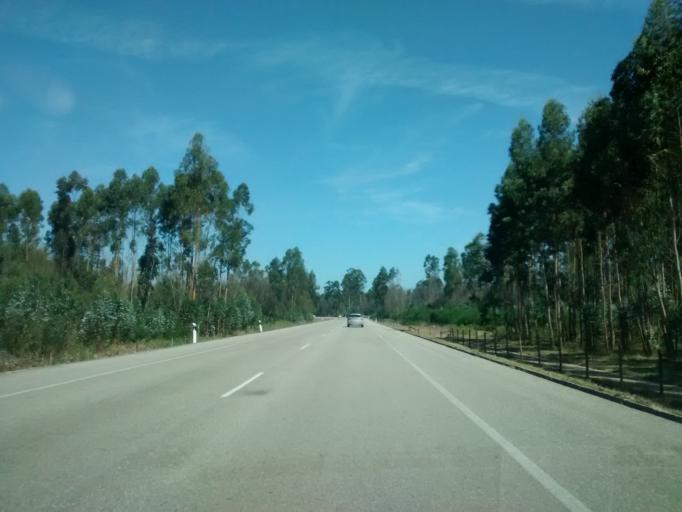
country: PT
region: Coimbra
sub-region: Mira
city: Mira
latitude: 40.4398
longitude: -8.7373
